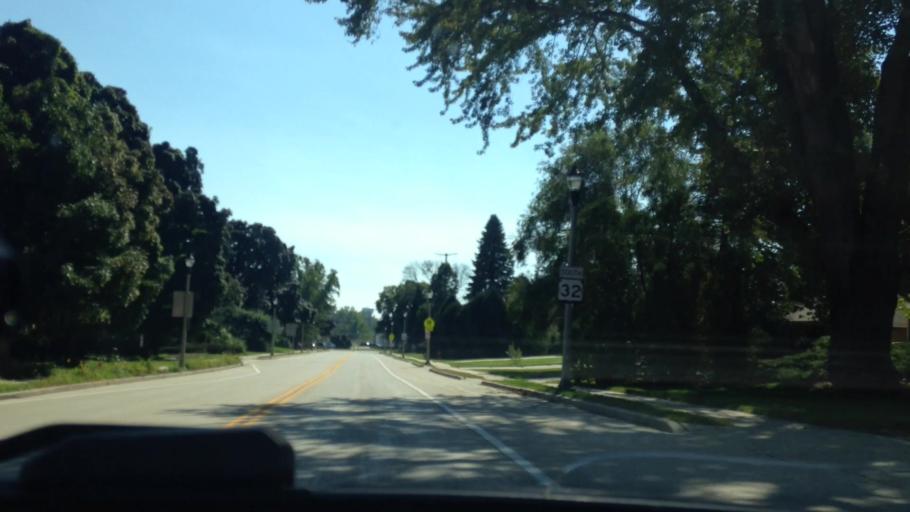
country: US
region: Wisconsin
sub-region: Ozaukee County
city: Port Washington
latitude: 43.3866
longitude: -87.8858
